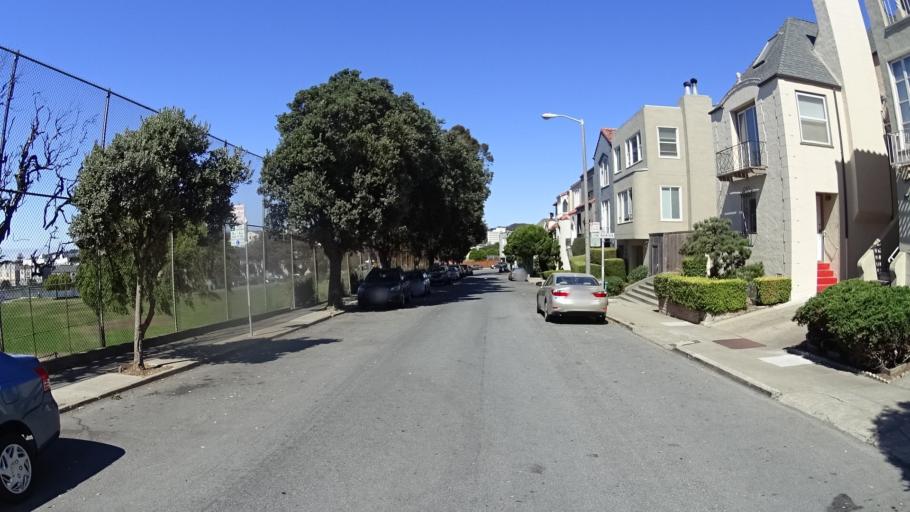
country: US
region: California
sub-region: San Francisco County
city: San Francisco
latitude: 37.7785
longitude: -122.4562
